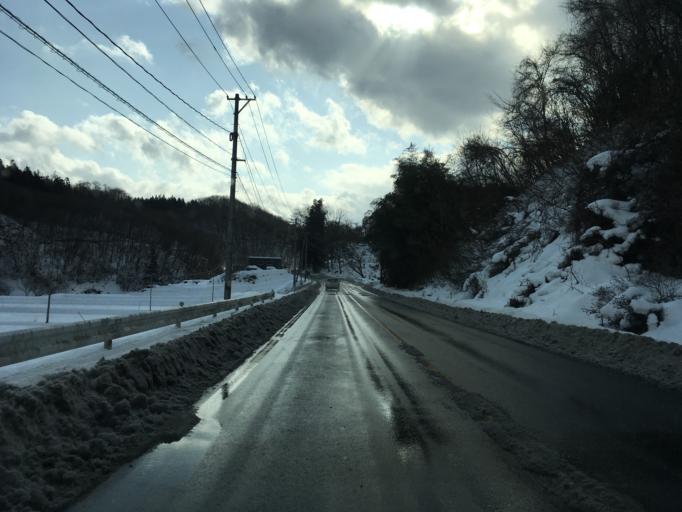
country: JP
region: Iwate
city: Ichinoseki
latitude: 38.9817
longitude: 141.3306
